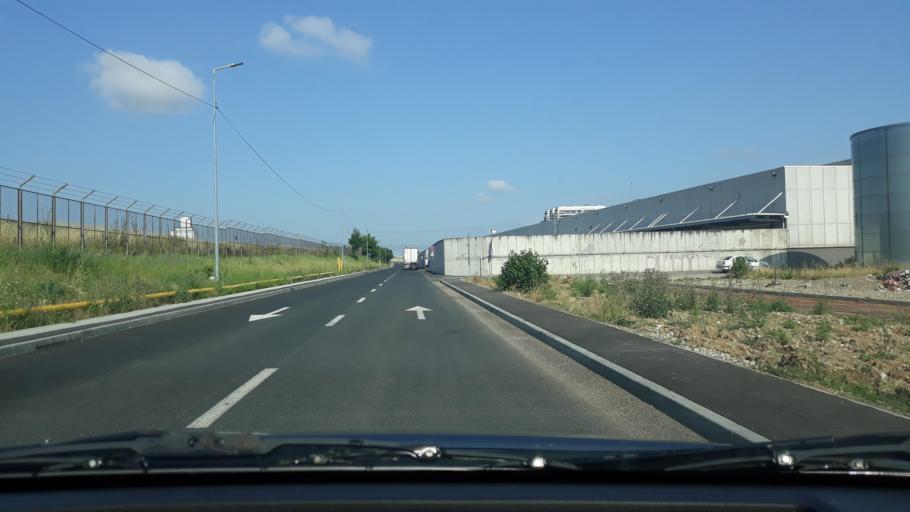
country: RO
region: Bihor
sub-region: Comuna Biharea
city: Oradea
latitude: 47.0396
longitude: 21.9052
